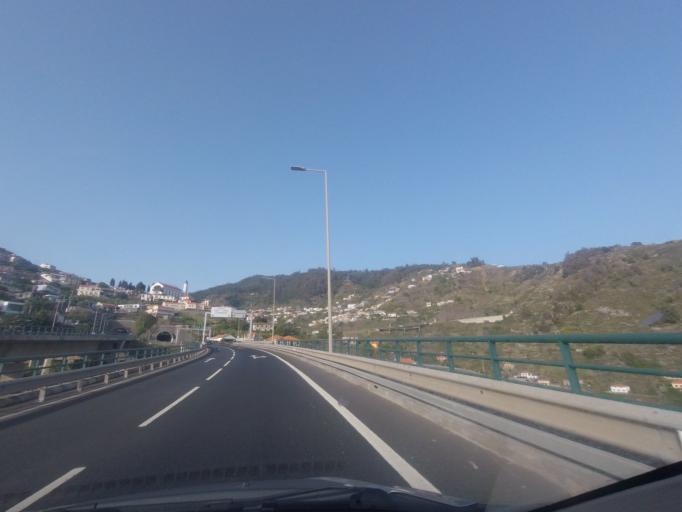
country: PT
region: Madeira
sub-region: Ribeira Brava
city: Campanario
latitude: 32.6654
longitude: -17.0340
